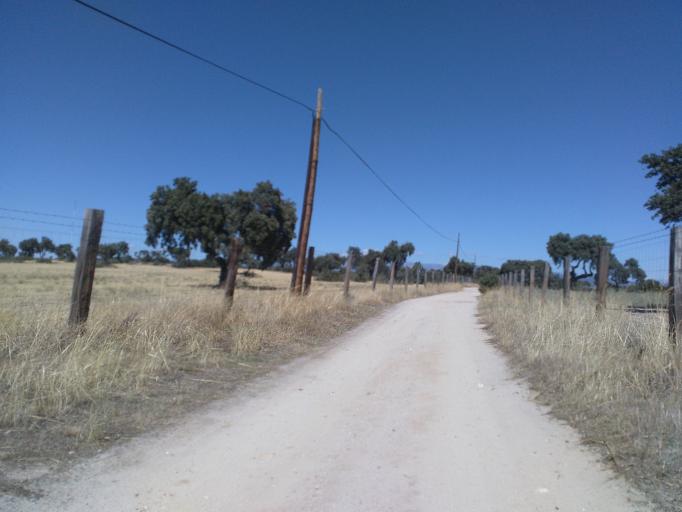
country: ES
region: Madrid
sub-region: Provincia de Madrid
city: Villanueva del Pardillo
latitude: 40.4565
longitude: -3.9565
